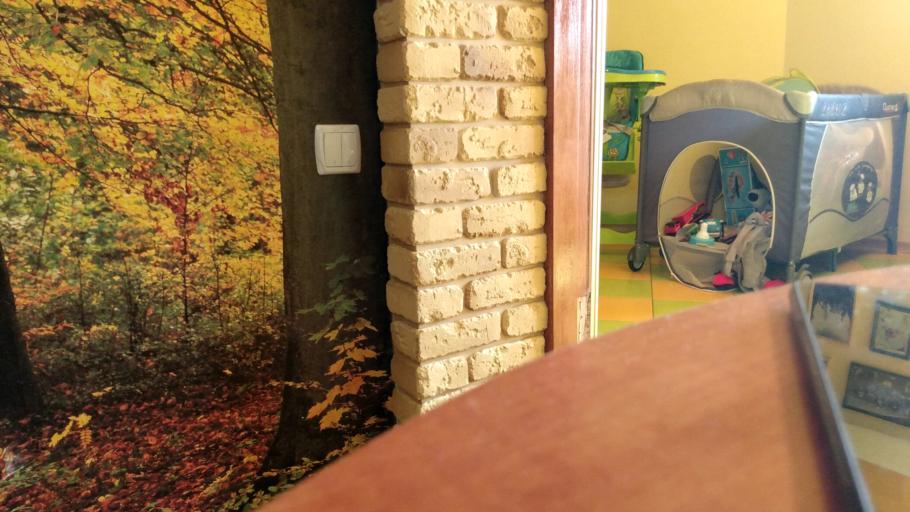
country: RU
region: Tverskaya
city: Vasil'yevskiy Mokh
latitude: 56.9787
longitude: 35.9177
